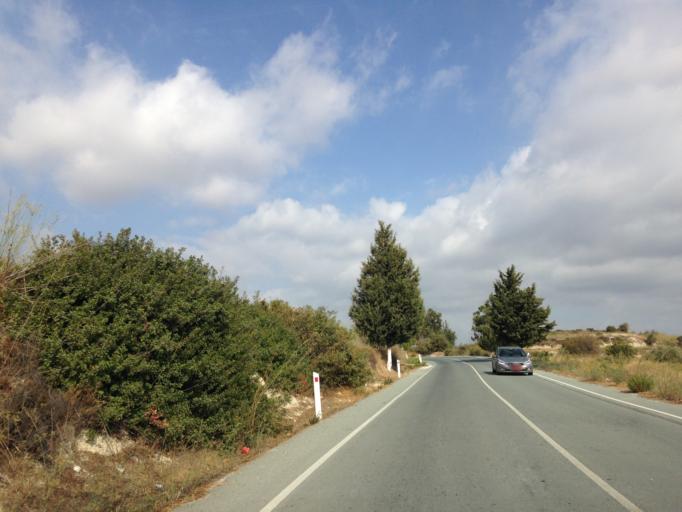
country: CY
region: Limassol
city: Pachna
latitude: 34.7941
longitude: 32.8015
